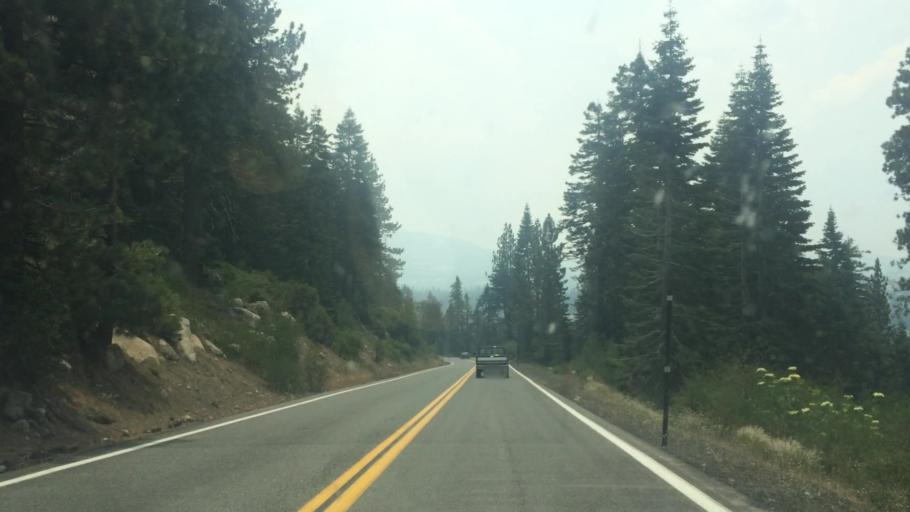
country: US
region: California
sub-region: El Dorado County
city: South Lake Tahoe
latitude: 38.6883
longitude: -120.1237
